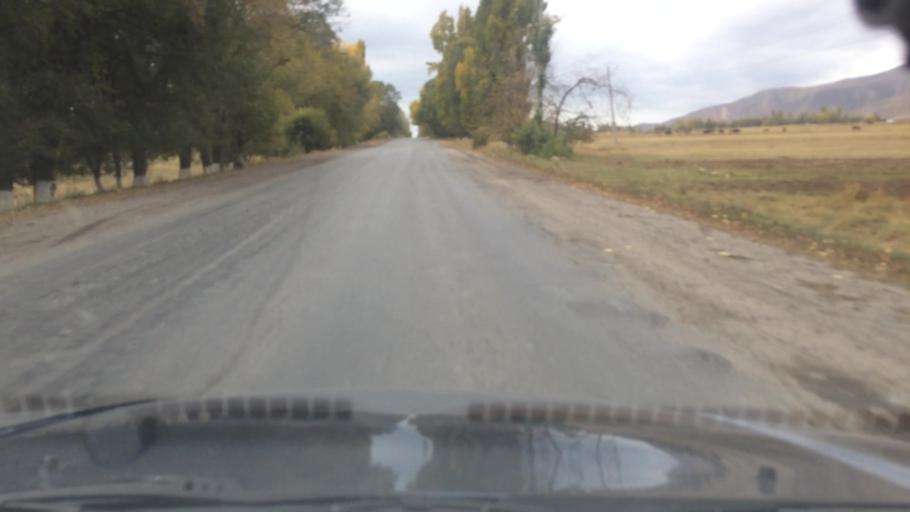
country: KG
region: Ysyk-Koel
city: Tyup
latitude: 42.7760
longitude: 78.2037
